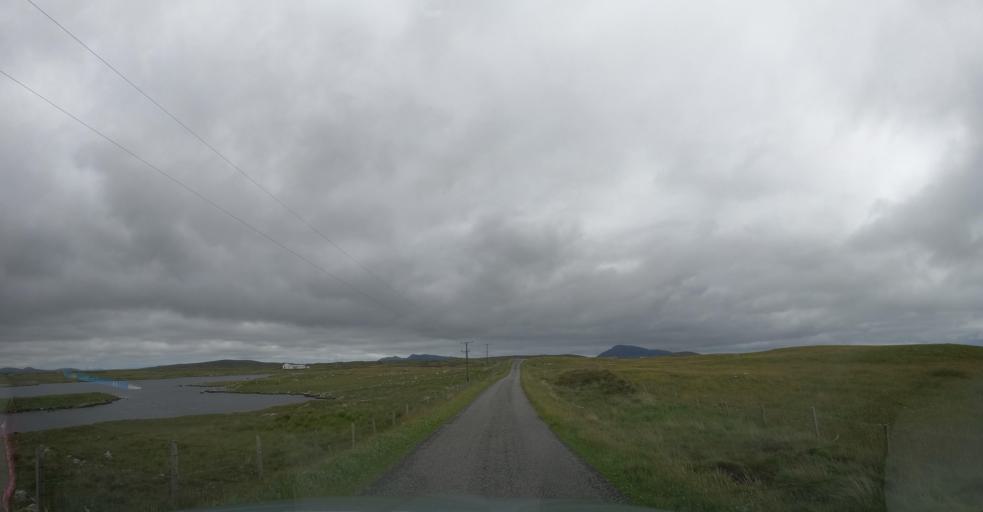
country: GB
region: Scotland
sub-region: Eilean Siar
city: Isle of North Uist
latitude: 57.5424
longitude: -7.3358
